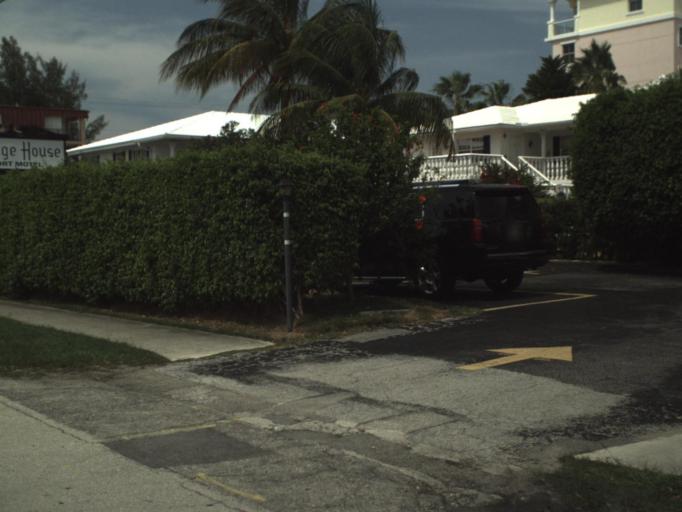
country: US
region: Florida
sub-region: Broward County
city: Hillsboro Beach
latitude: 26.3121
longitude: -80.0777
